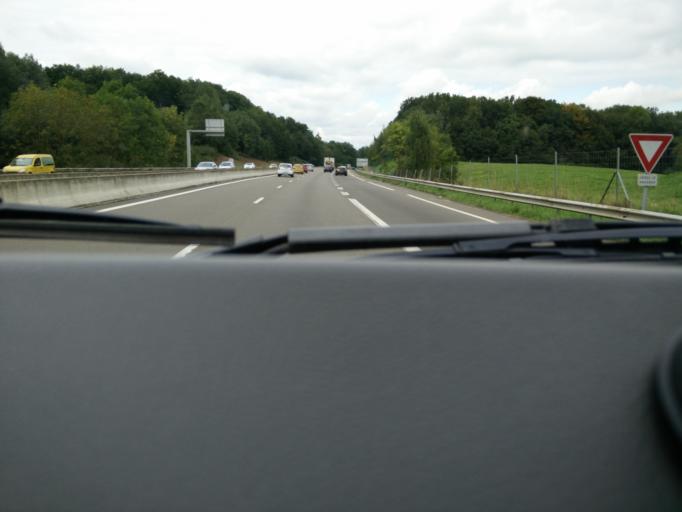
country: FR
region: Champagne-Ardenne
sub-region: Departement des Ardennes
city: La Francheville
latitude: 49.7414
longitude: 4.7087
